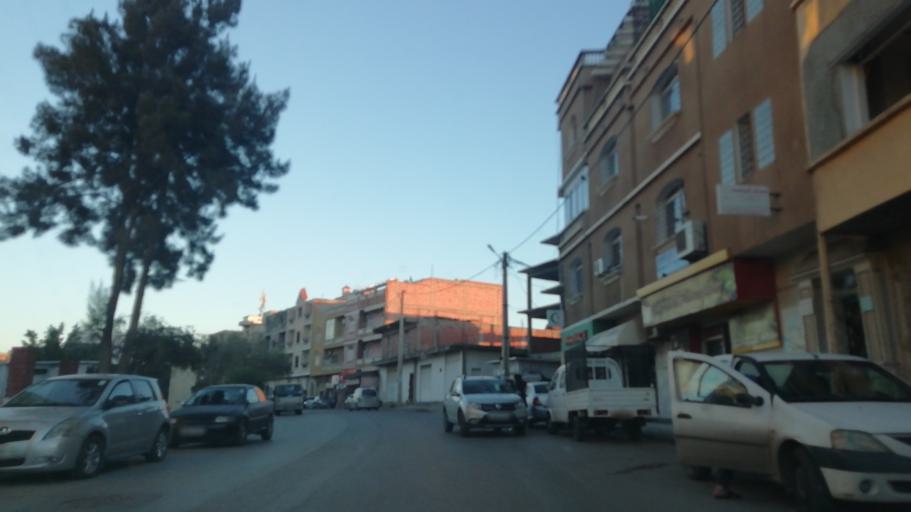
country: DZ
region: Oran
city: Oran
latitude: 35.6986
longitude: -0.5971
